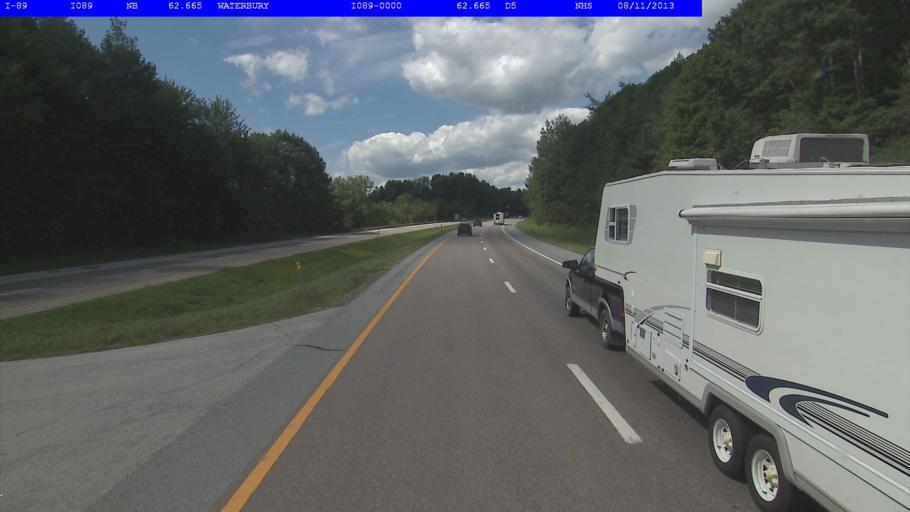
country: US
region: Vermont
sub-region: Washington County
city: Waterbury
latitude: 44.3295
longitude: -72.7435
